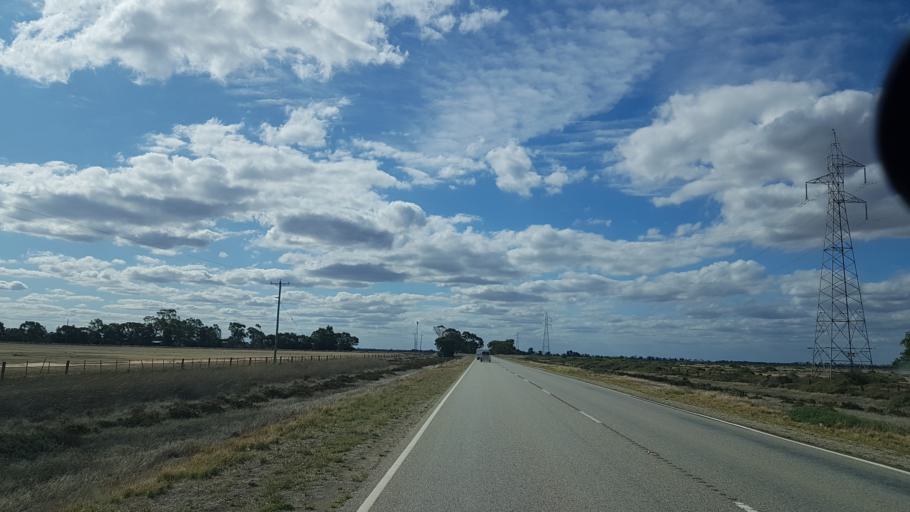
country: AU
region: Victoria
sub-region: Swan Hill
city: Swan Hill
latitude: -35.8834
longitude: 143.9406
